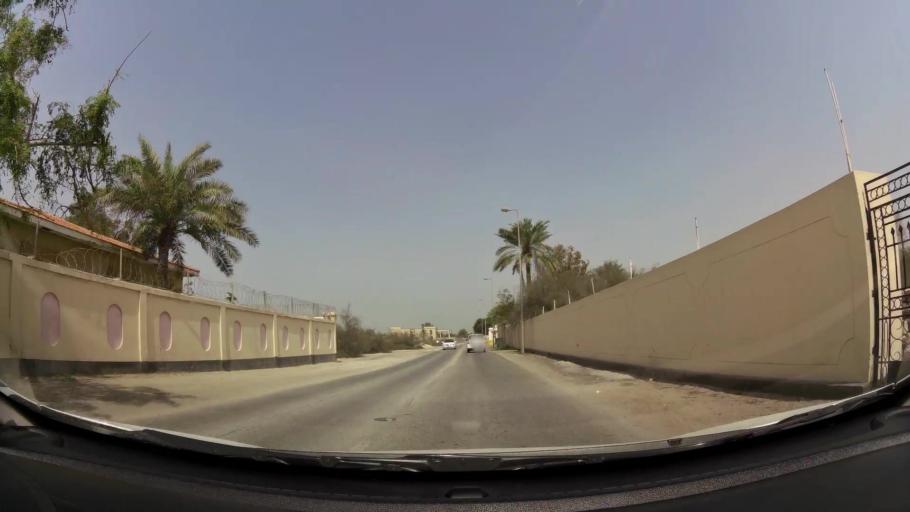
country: BH
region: Manama
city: Jidd Hafs
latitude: 26.2203
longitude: 50.4783
